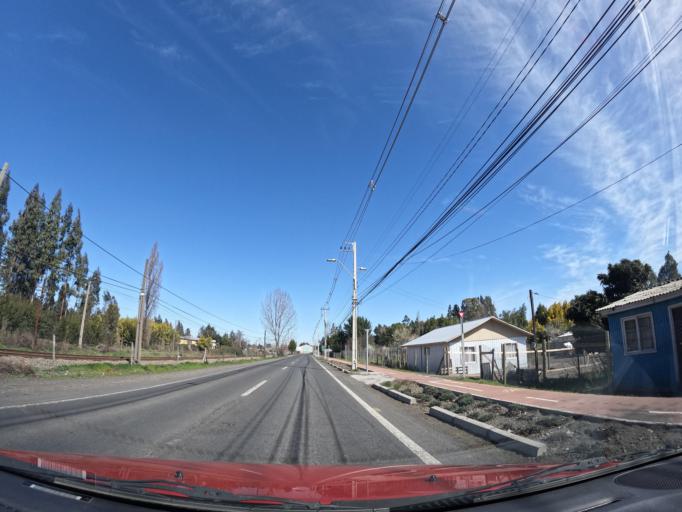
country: CL
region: Biobio
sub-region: Provincia de Biobio
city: Cabrero
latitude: -37.0782
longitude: -72.4343
